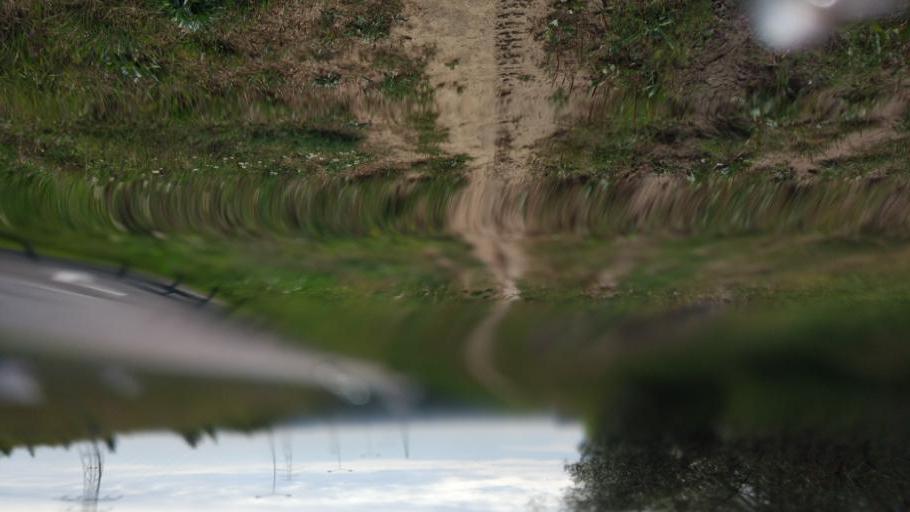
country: PL
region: Masovian Voivodeship
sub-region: Plock
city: Plock
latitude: 52.5302
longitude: 19.7384
